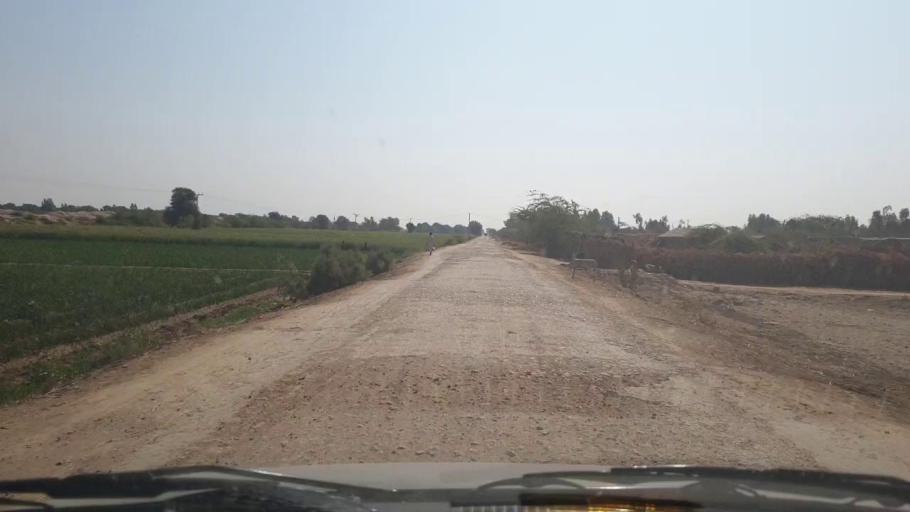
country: PK
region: Sindh
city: Samaro
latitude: 25.2736
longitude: 69.3436
